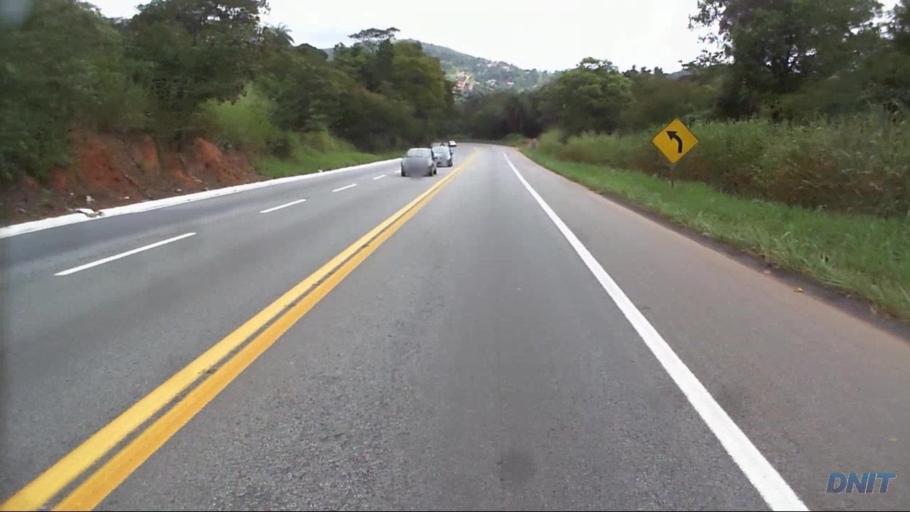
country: BR
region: Minas Gerais
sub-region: Santa Luzia
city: Santa Luzia
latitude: -19.7874
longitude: -43.7406
